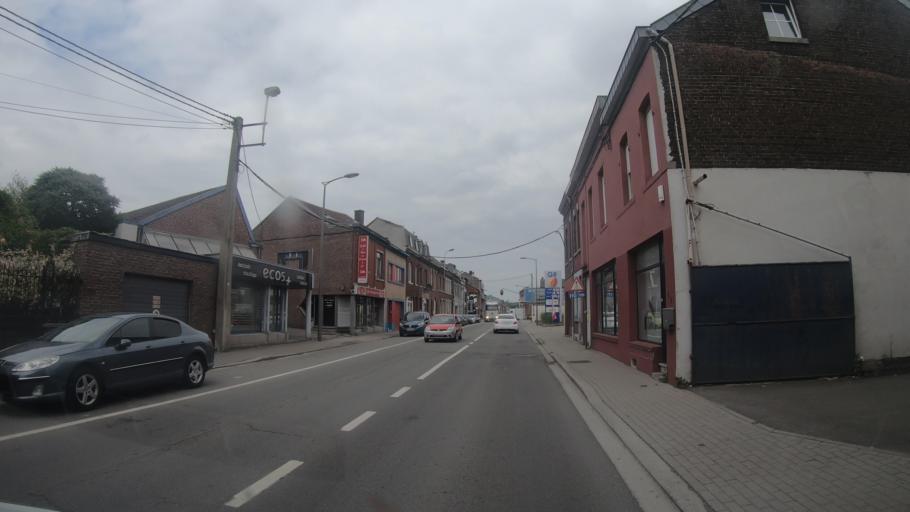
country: BE
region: Wallonia
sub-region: Province de Liege
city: Herstal
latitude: 50.6745
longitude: 5.6399
